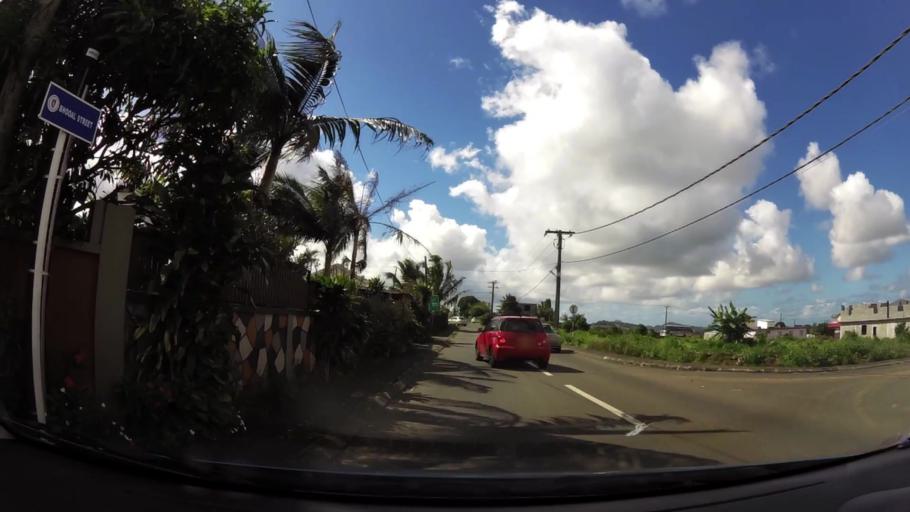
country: MU
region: Grand Port
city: Rose Belle
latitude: -20.3965
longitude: 57.5914
